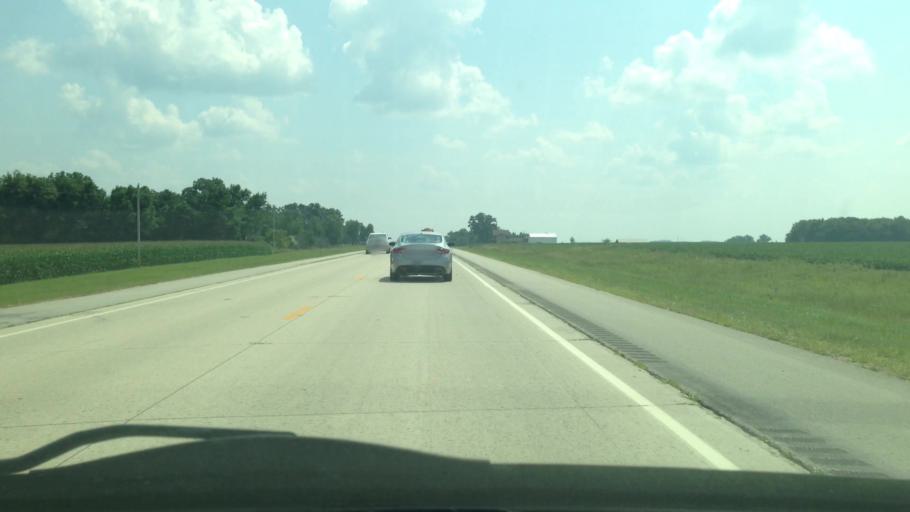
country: US
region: Minnesota
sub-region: Fillmore County
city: Spring Valley
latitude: 43.5203
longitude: -92.3694
